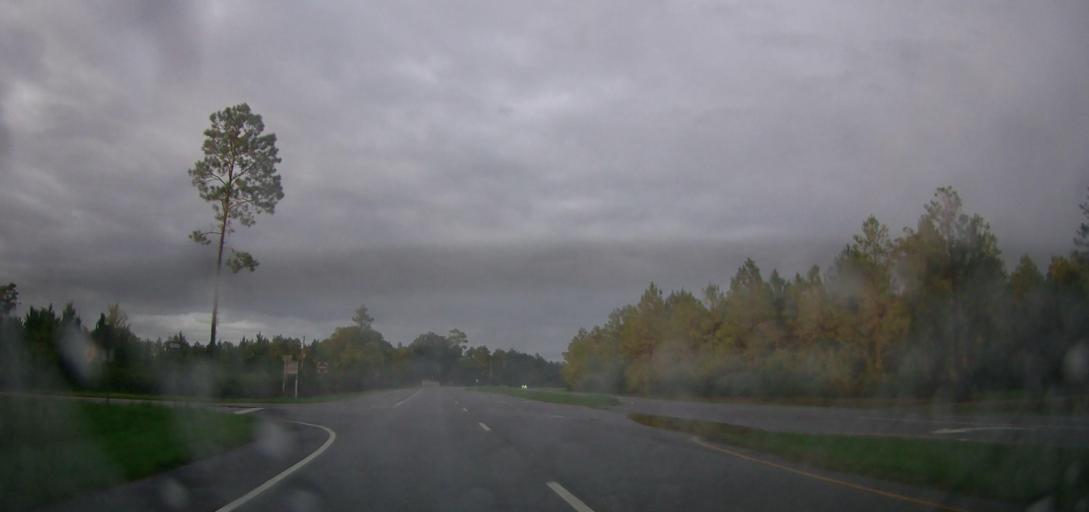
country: US
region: Georgia
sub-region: Clinch County
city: Homerville
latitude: 30.9986
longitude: -82.8636
